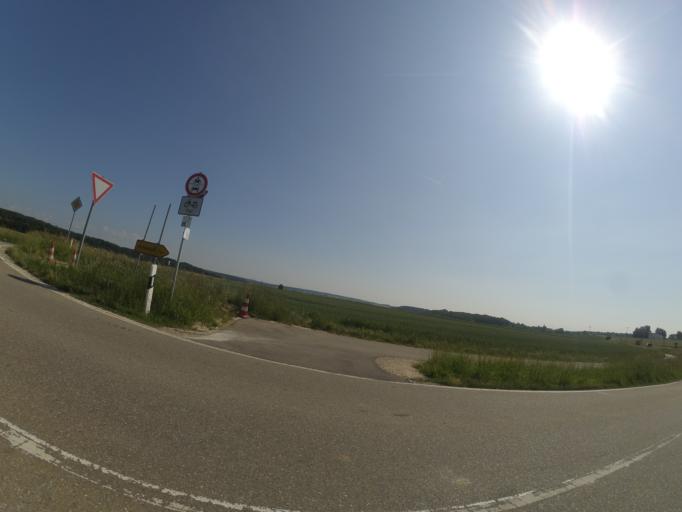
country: DE
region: Baden-Wuerttemberg
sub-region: Tuebingen Region
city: Beimerstetten
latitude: 48.4832
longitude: 9.9921
